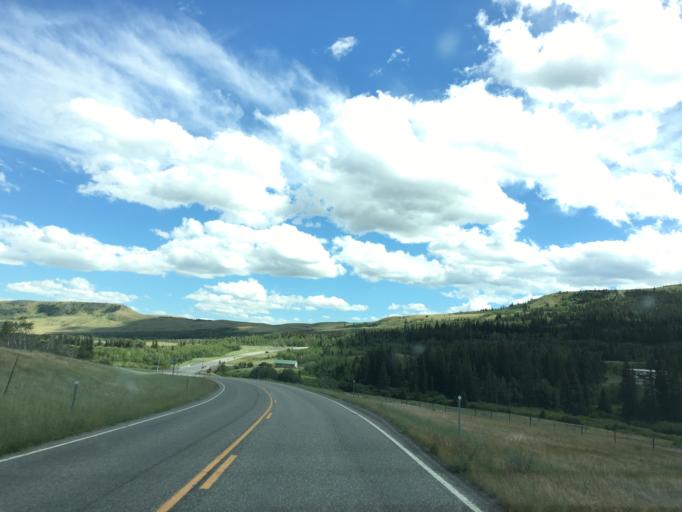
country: US
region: Montana
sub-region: Glacier County
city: Browning
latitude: 48.6110
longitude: -113.2902
